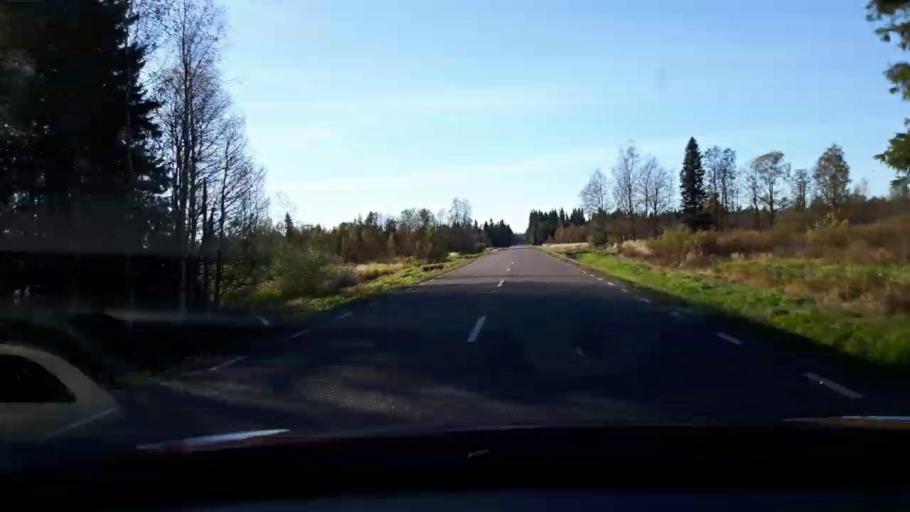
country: SE
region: Jaemtland
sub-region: Stroemsunds Kommun
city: Stroemsund
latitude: 63.8458
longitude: 15.2964
